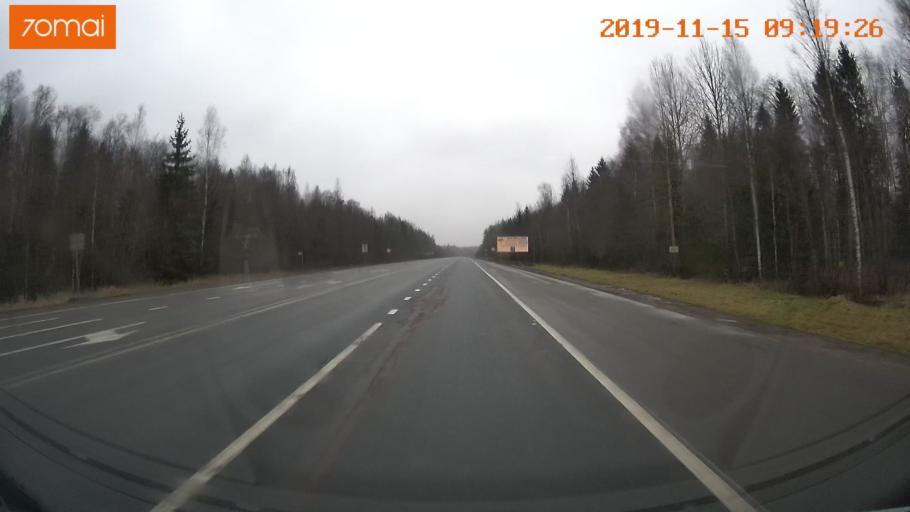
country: RU
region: Vologda
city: Tonshalovo
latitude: 59.2837
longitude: 38.0159
